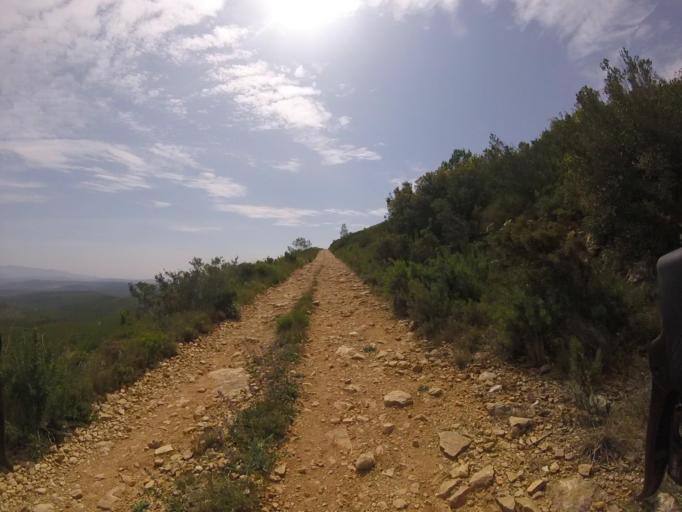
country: ES
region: Valencia
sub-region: Provincia de Castello
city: Cuevas de Vinroma
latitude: 40.2641
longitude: 0.1124
